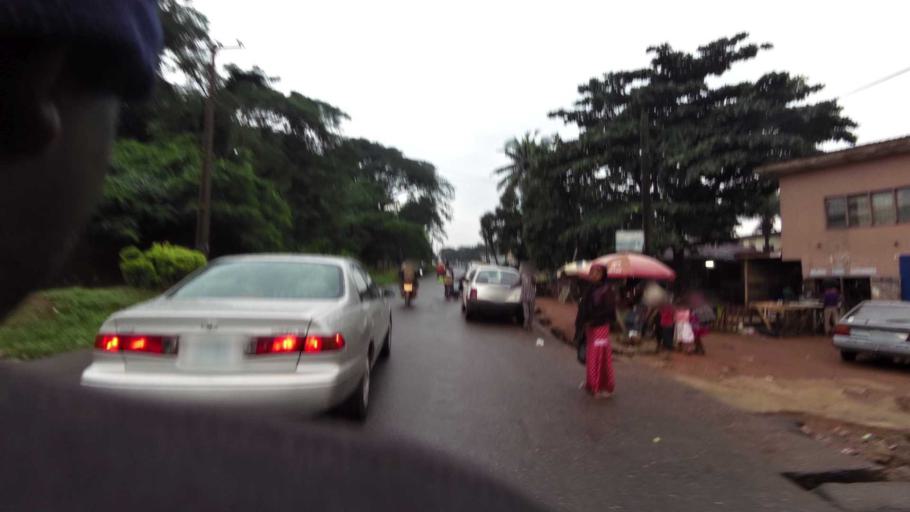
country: NG
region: Oyo
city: Ibadan
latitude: 7.4040
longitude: 3.9264
